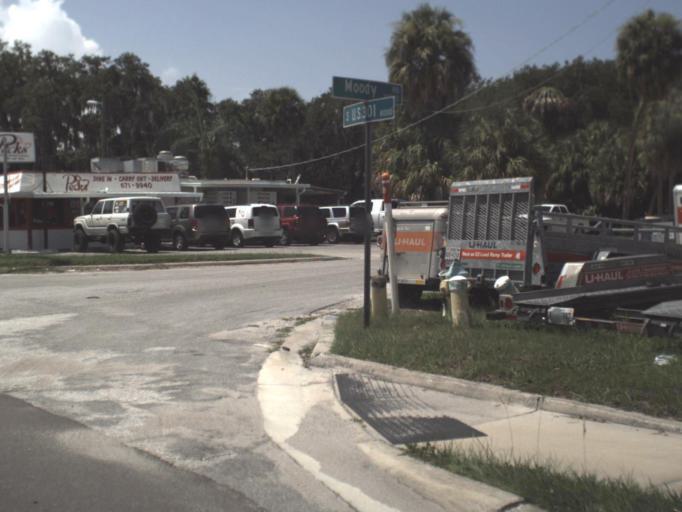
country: US
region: Florida
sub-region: Hillsborough County
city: Riverview
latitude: 27.8710
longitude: -82.3268
